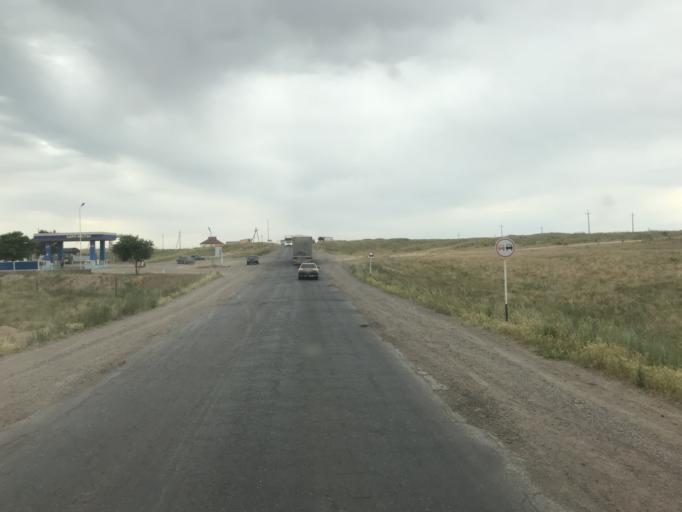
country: UZ
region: Toshkent
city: Chinoz
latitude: 41.1326
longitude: 68.7202
